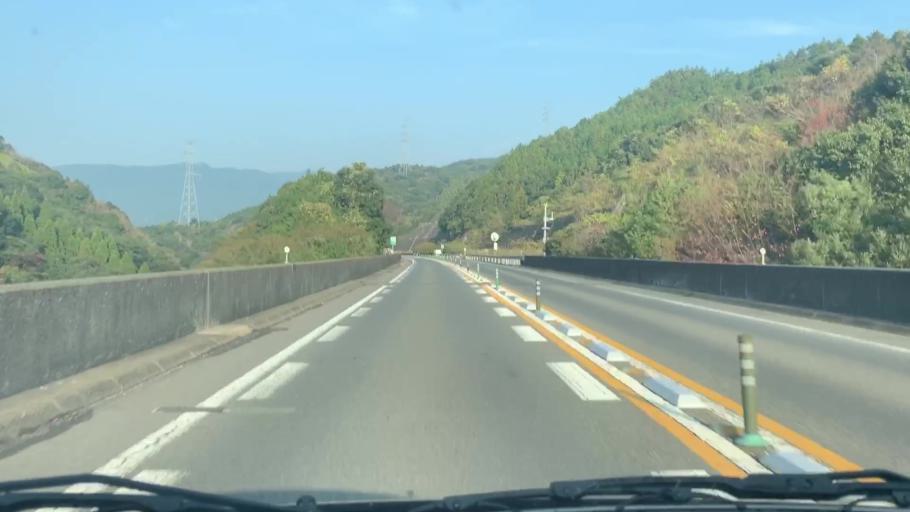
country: JP
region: Saga Prefecture
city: Imaricho-ko
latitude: 33.1626
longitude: 129.8641
